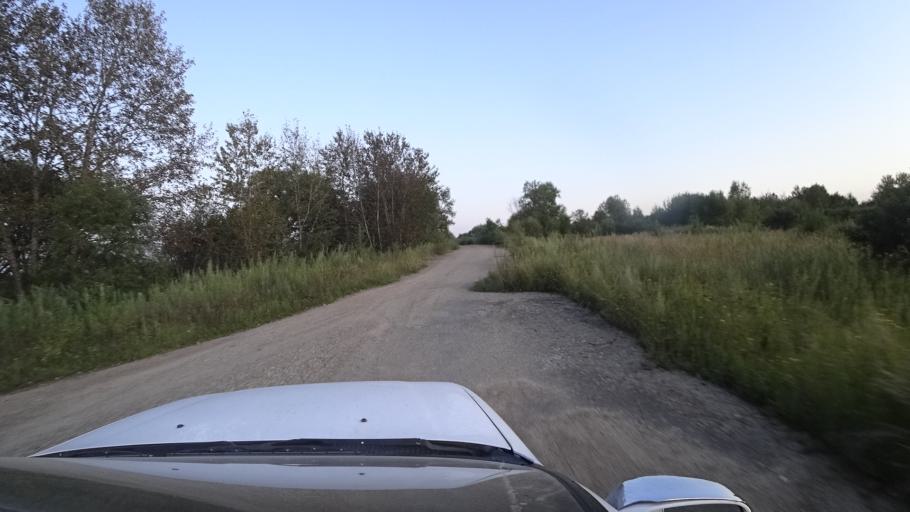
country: RU
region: Primorskiy
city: Dal'nerechensk
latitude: 45.9486
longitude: 133.7622
